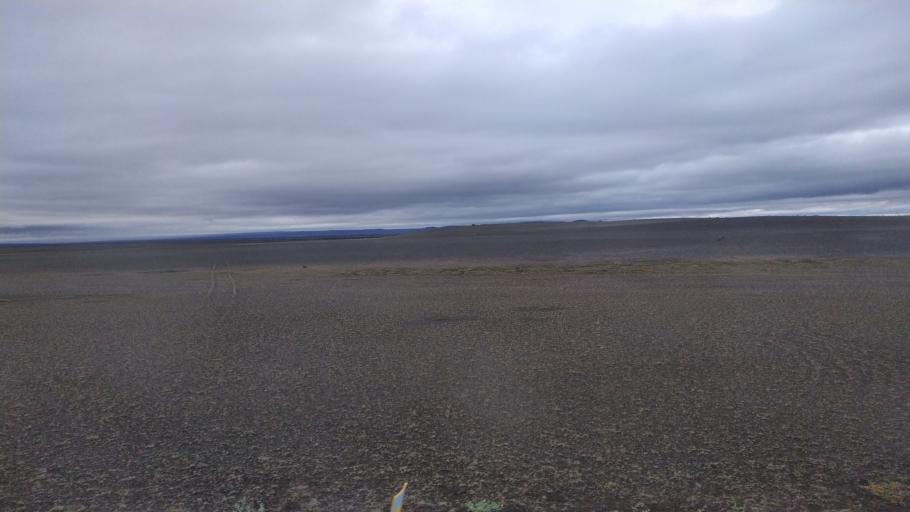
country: IS
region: Northeast
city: Laugar
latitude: 65.6147
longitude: -16.1609
